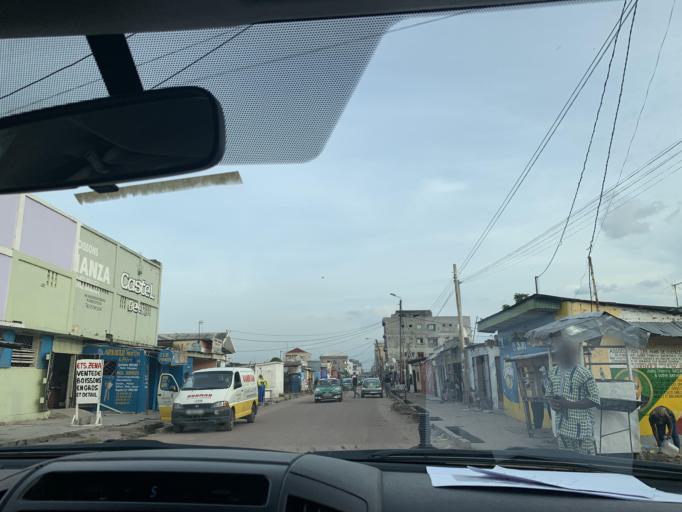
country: CG
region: Brazzaville
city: Brazzaville
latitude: -4.2525
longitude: 15.2862
